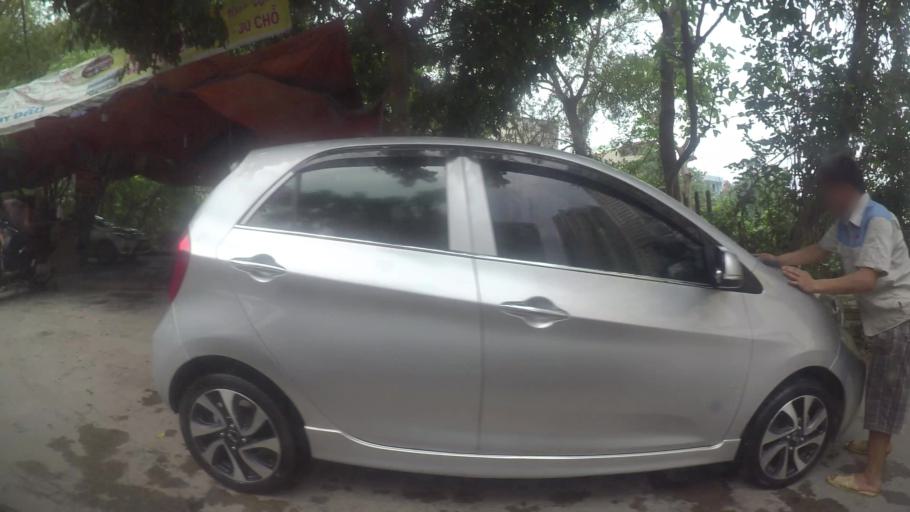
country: VN
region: Ha Noi
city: Ha Dong
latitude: 20.9712
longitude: 105.7576
